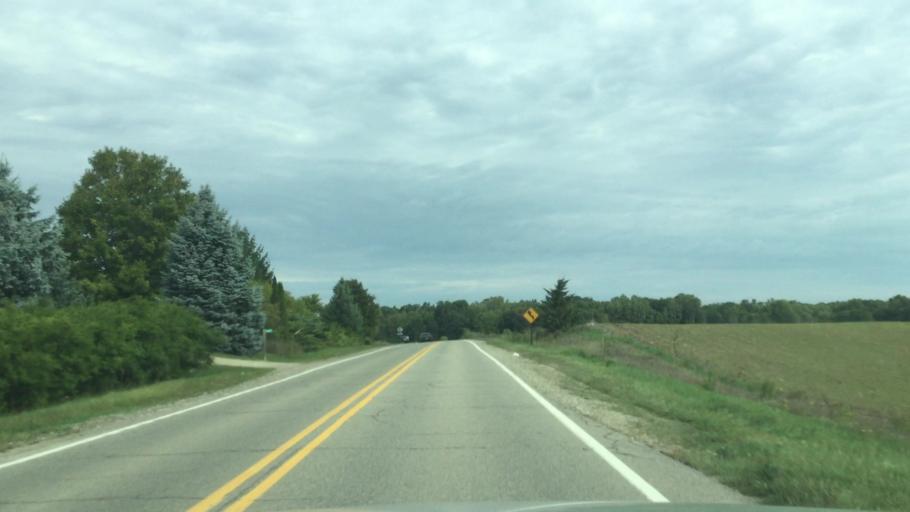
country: US
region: Michigan
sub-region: Livingston County
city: Howell
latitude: 42.6896
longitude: -83.8779
